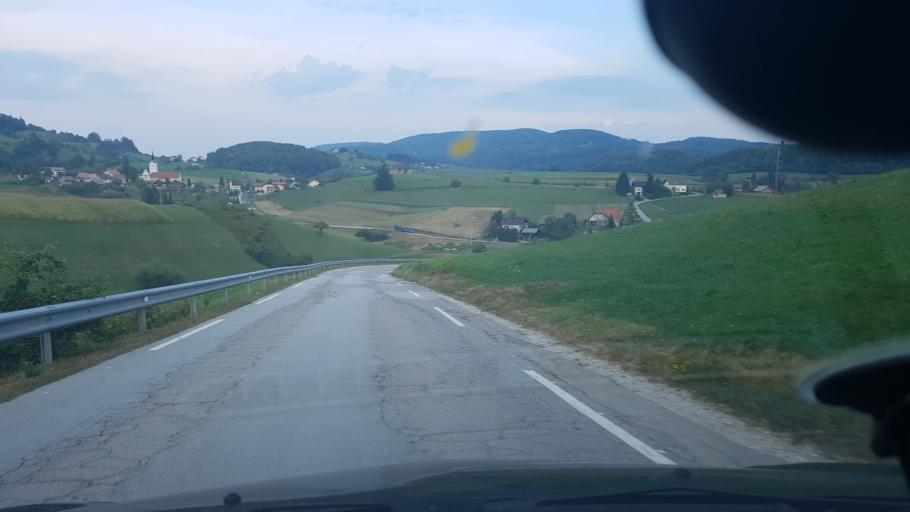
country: SI
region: Kozje
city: Kozje
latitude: 46.0350
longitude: 15.5314
